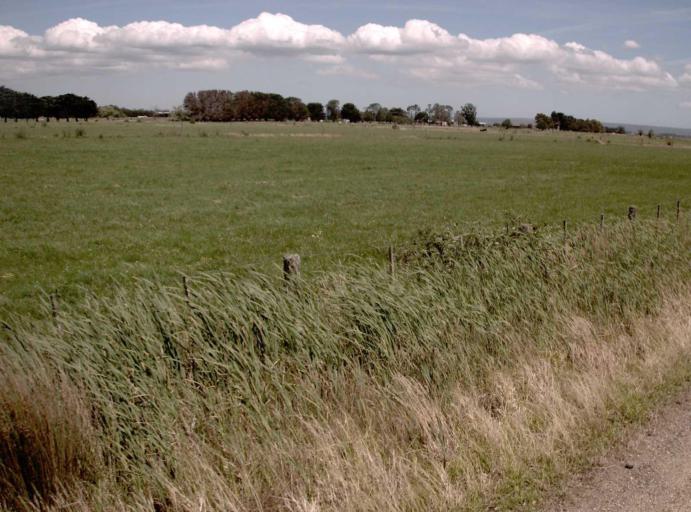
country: AU
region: Victoria
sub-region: Wellington
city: Heyfield
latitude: -38.0674
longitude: 146.8714
